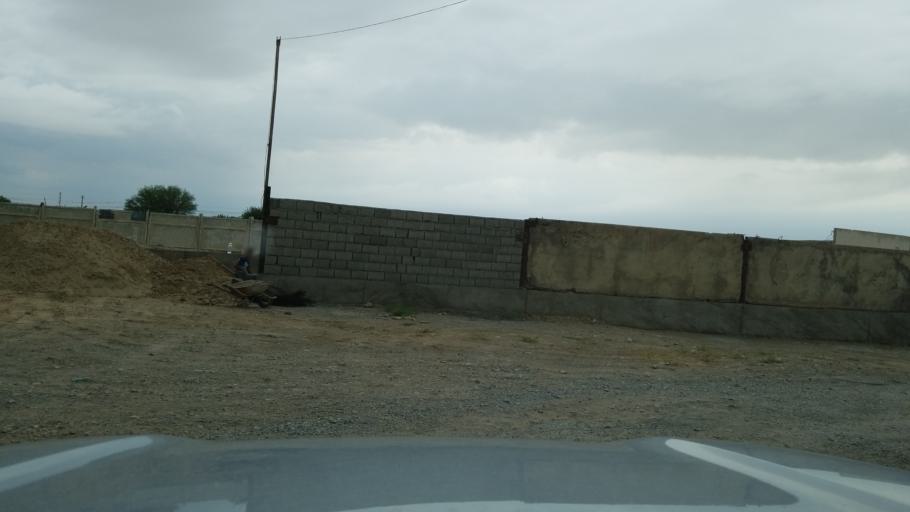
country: TM
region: Balkan
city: Serdar
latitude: 38.9690
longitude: 56.2828
